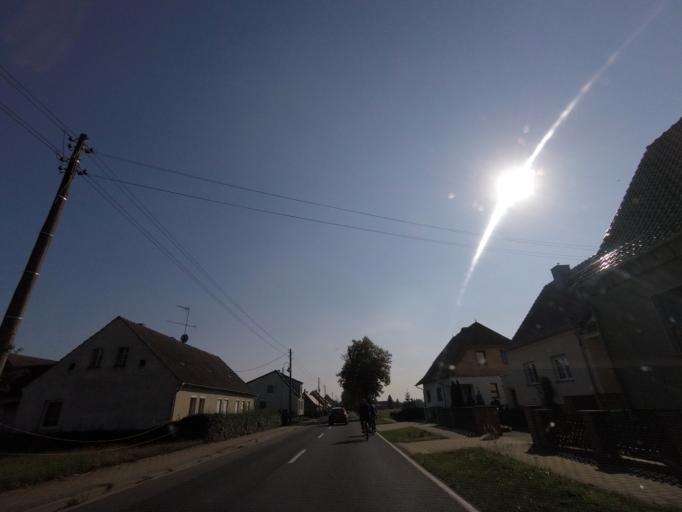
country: DE
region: Saxony-Anhalt
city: Jessen
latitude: 51.8566
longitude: 13.0251
